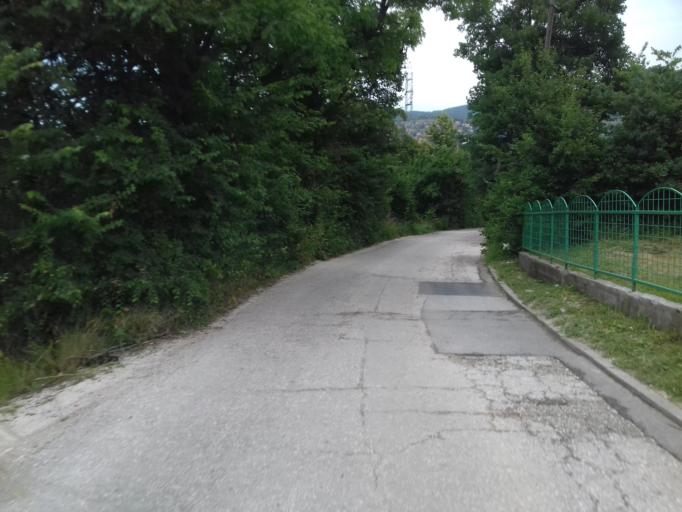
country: BA
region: Federation of Bosnia and Herzegovina
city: Hotonj
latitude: 43.8937
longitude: 18.3622
